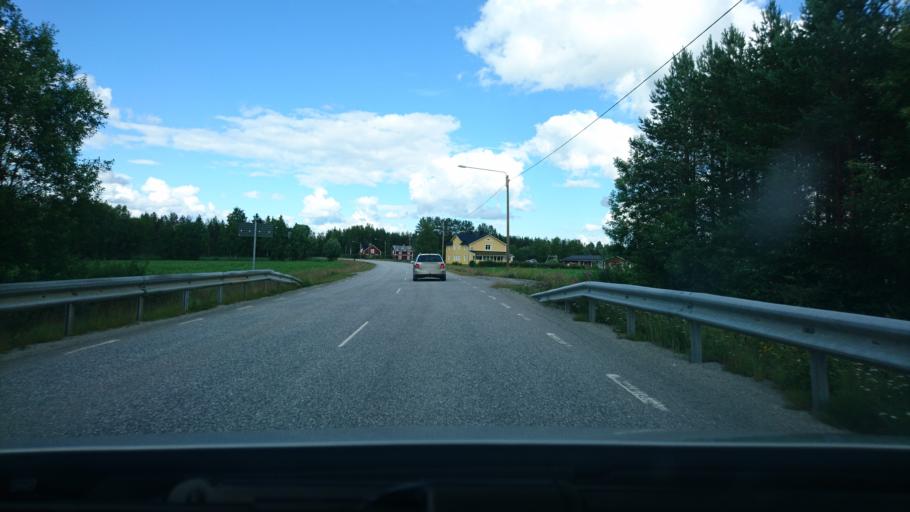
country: SE
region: Vaesterbotten
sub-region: Asele Kommun
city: Asele
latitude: 64.0103
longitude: 17.2874
